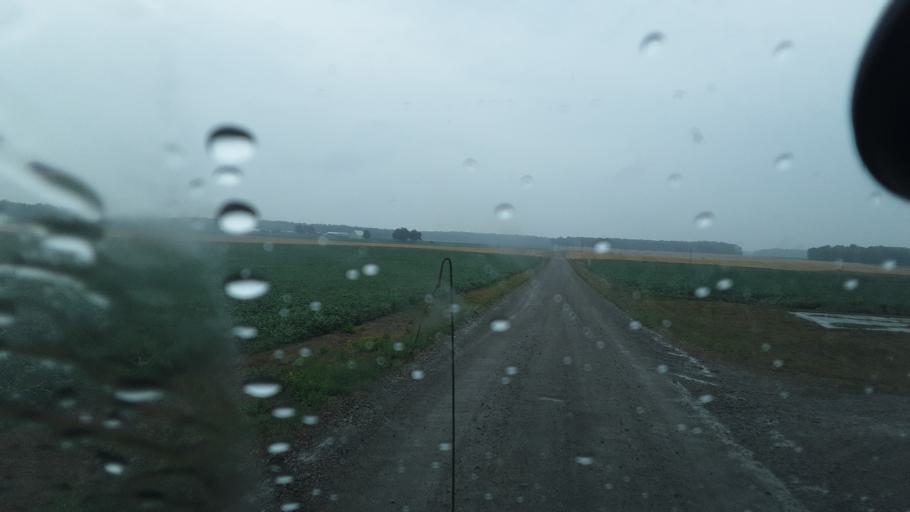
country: US
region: Indiana
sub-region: DeKalb County
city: Butler
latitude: 41.4188
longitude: -84.8130
